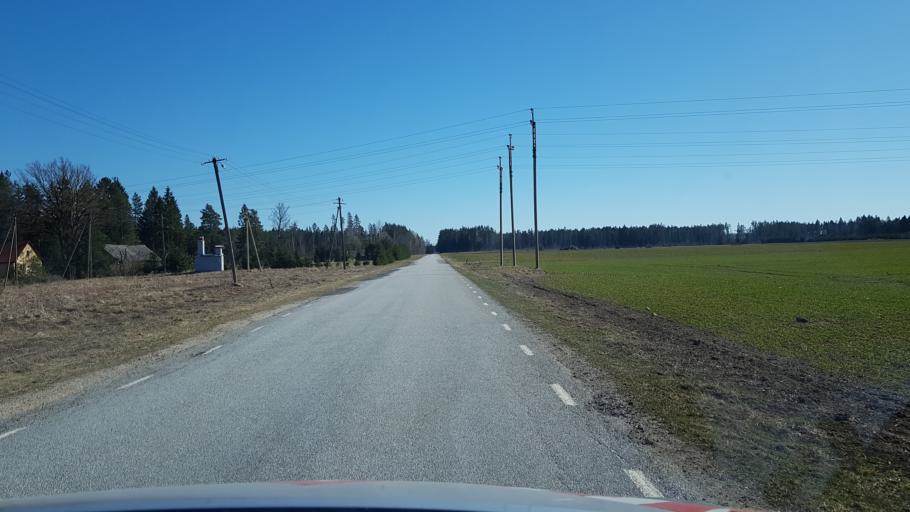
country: EE
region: Laeaene-Virumaa
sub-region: Viru-Nigula vald
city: Kunda
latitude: 59.3893
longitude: 26.5705
